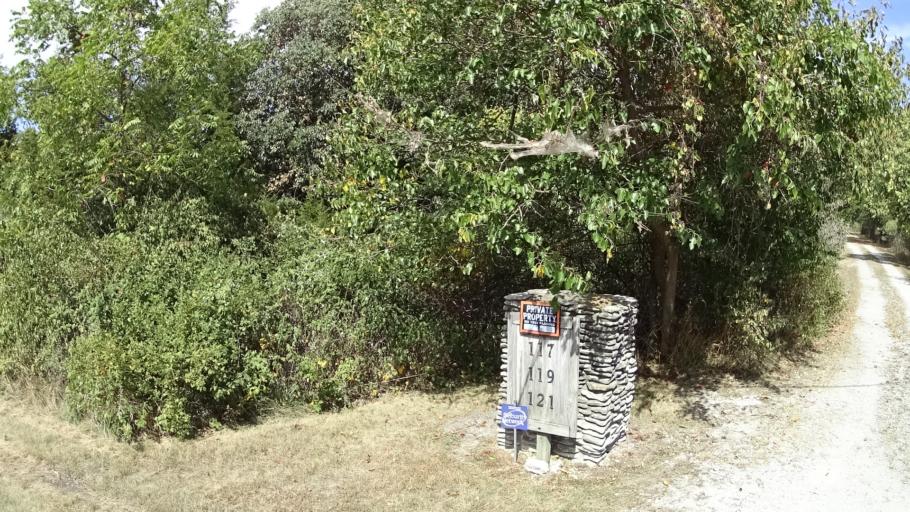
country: US
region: Ohio
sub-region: Erie County
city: Sandusky
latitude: 41.6081
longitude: -82.6931
